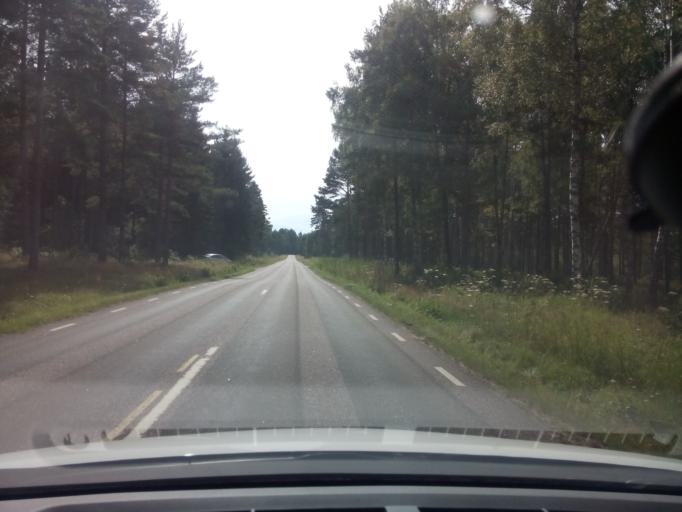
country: SE
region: Soedermanland
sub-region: Oxelosunds Kommun
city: Oxelosund
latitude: 58.7607
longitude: 17.3274
